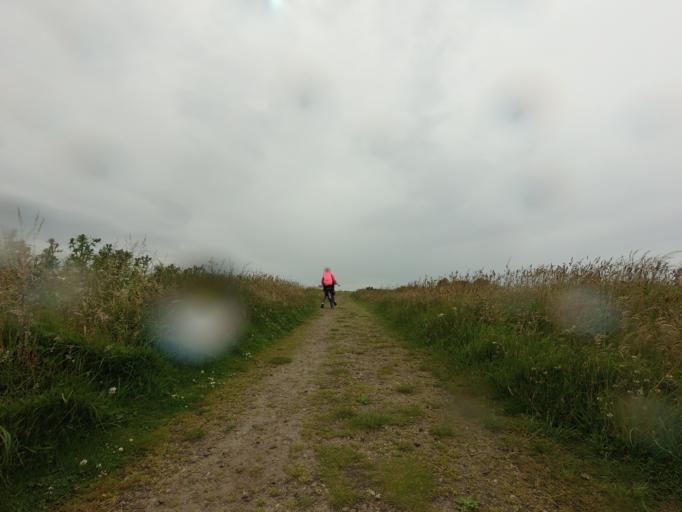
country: GB
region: Scotland
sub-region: Moray
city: Portknockie
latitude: 57.7027
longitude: -2.8793
